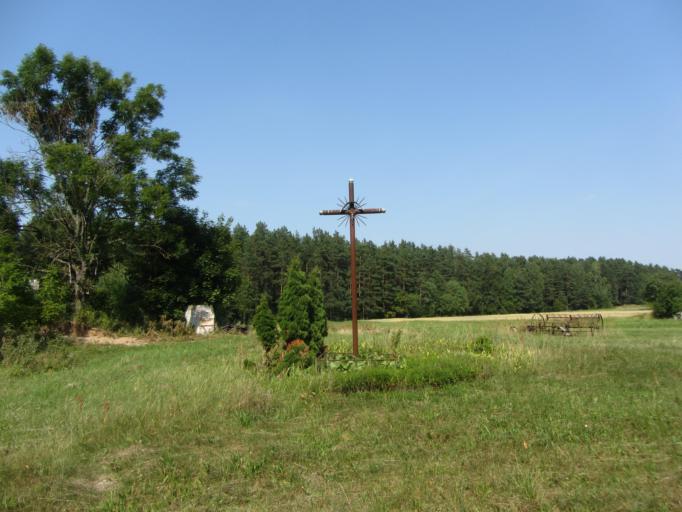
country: LT
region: Alytaus apskritis
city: Druskininkai
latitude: 54.1457
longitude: 23.8778
